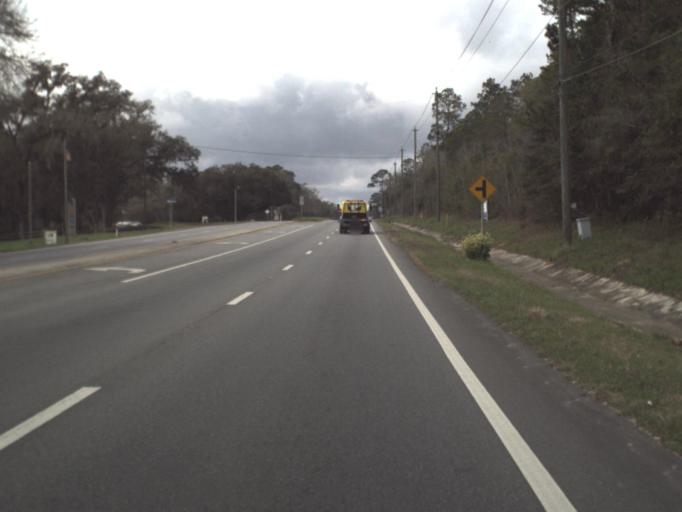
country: US
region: Florida
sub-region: Leon County
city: Tallahassee
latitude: 30.4289
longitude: -84.2042
